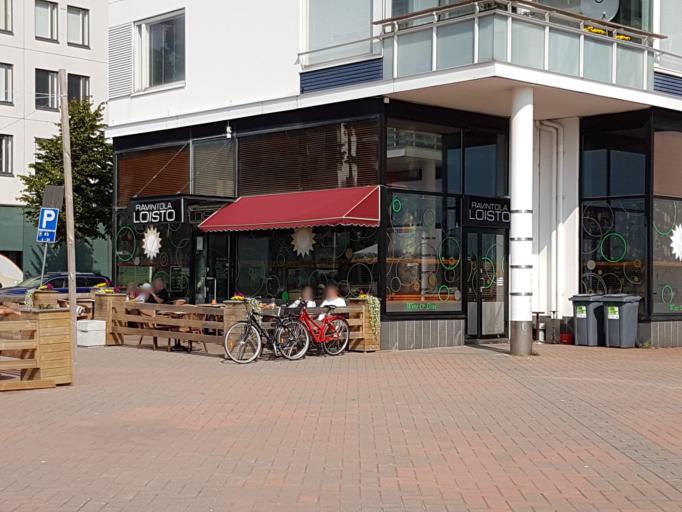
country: FI
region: Uusimaa
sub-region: Helsinki
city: Vantaa
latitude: 60.2011
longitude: 25.1500
